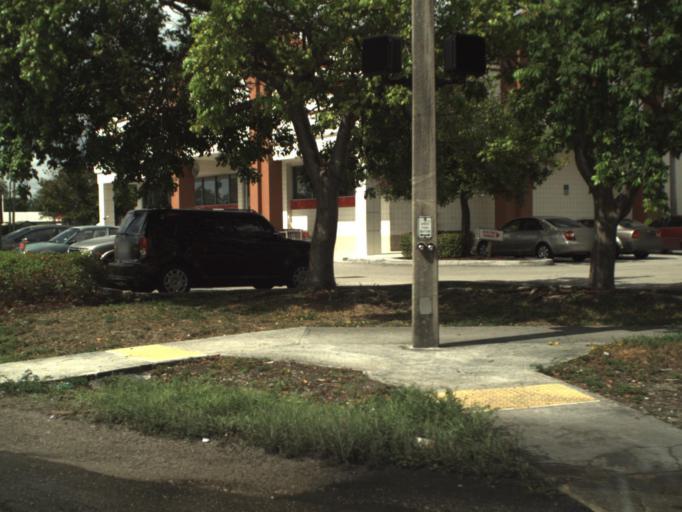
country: US
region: Florida
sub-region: Broward County
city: Pembroke Pines
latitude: 26.0026
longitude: -80.2074
